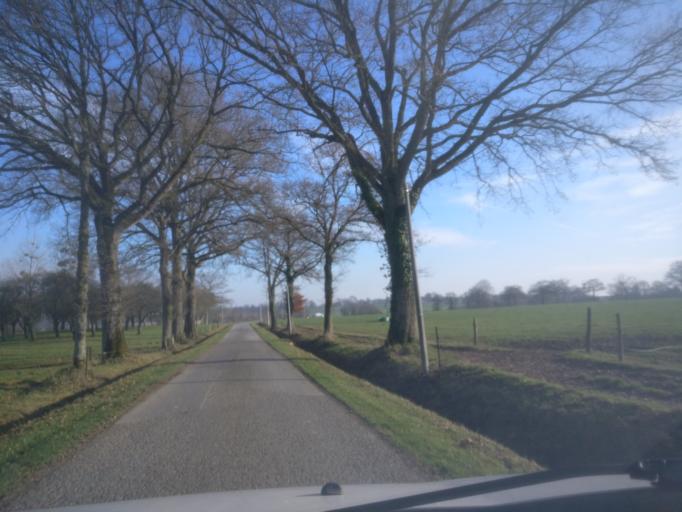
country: FR
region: Brittany
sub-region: Departement d'Ille-et-Vilaine
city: Livre-sur-Changeon
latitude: 48.2165
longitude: -1.3117
